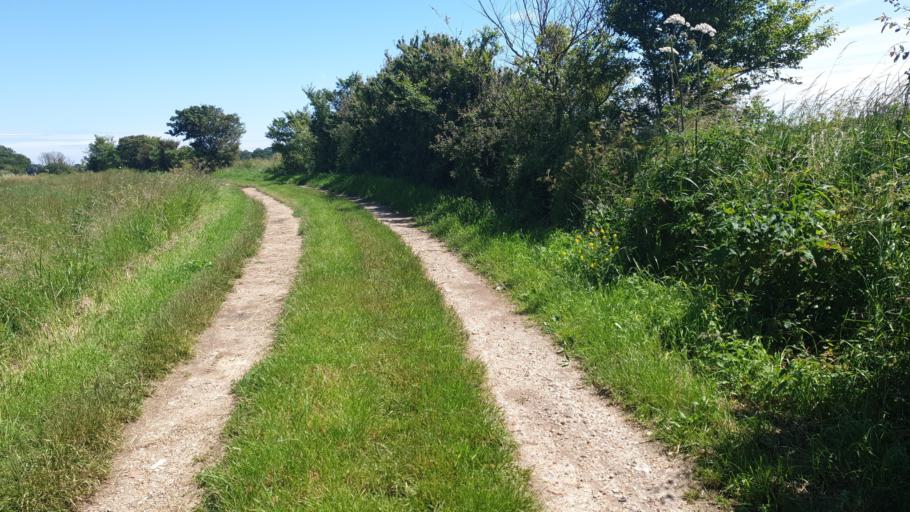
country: GB
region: England
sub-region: Essex
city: Saint Osyth
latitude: 51.7920
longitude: 1.1065
